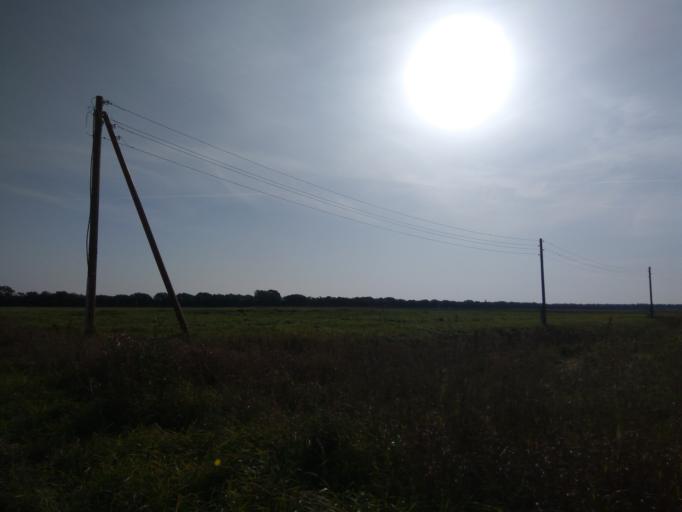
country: LV
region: Ventspils
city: Ventspils
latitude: 57.3643
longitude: 21.6388
